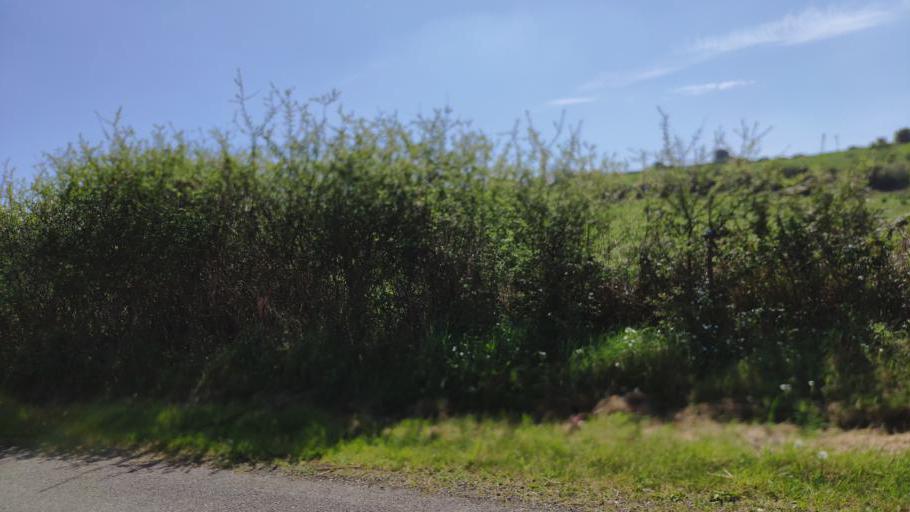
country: IE
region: Munster
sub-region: County Cork
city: Blarney
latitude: 51.9132
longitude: -8.5218
